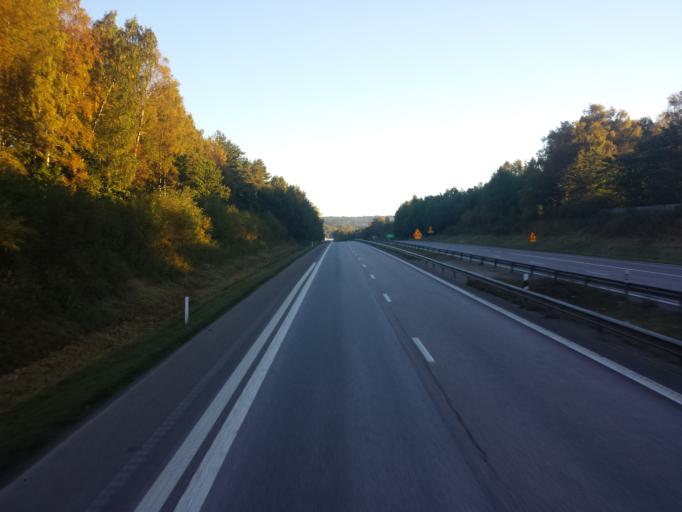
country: SE
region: Halland
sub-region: Kungsbacka Kommun
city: Kungsbacka
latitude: 57.4921
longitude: 12.0477
